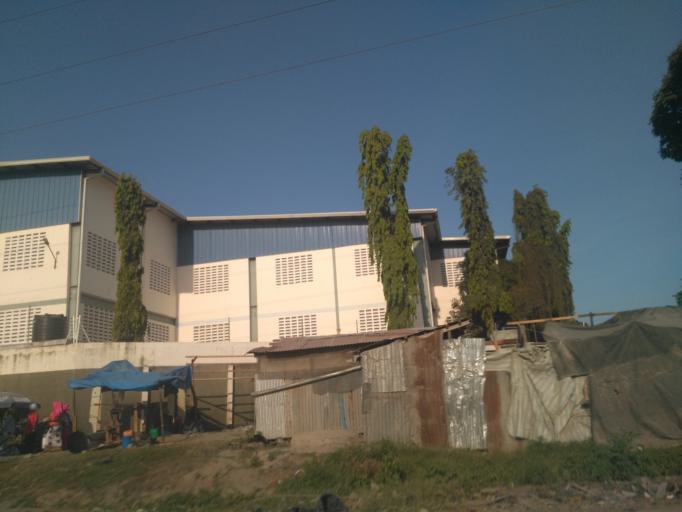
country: TZ
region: Pwani
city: Vikindu
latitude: -6.9195
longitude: 39.2659
